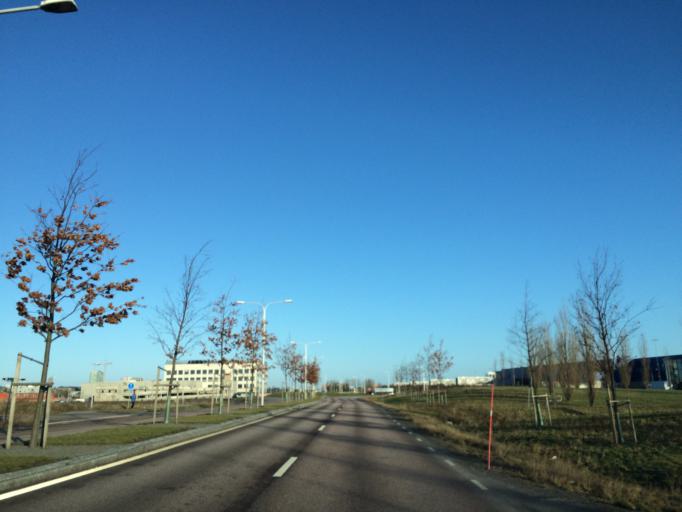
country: SE
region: Skane
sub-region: Malmo
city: Bunkeflostrand
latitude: 55.5496
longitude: 12.9827
